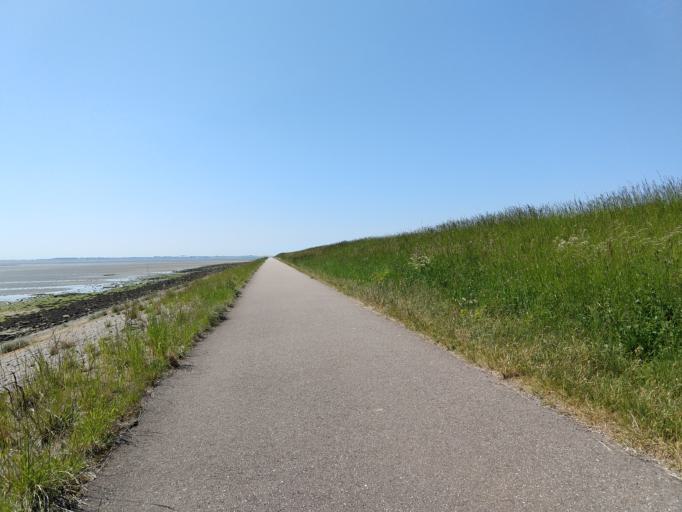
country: NL
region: Zeeland
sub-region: Gemeente Reimerswaal
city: Yerseke
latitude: 51.5763
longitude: 3.9947
